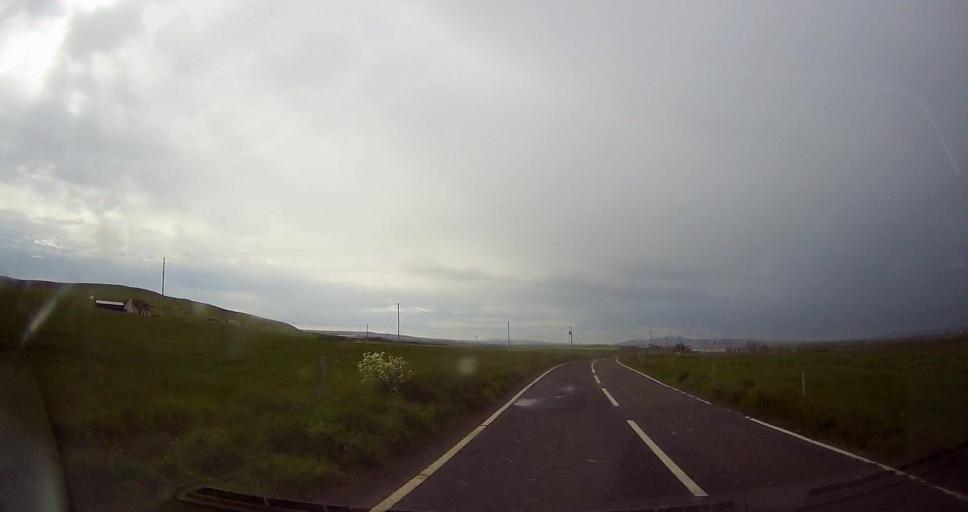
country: GB
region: Scotland
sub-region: Orkney Islands
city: Stromness
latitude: 59.0935
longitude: -3.2632
